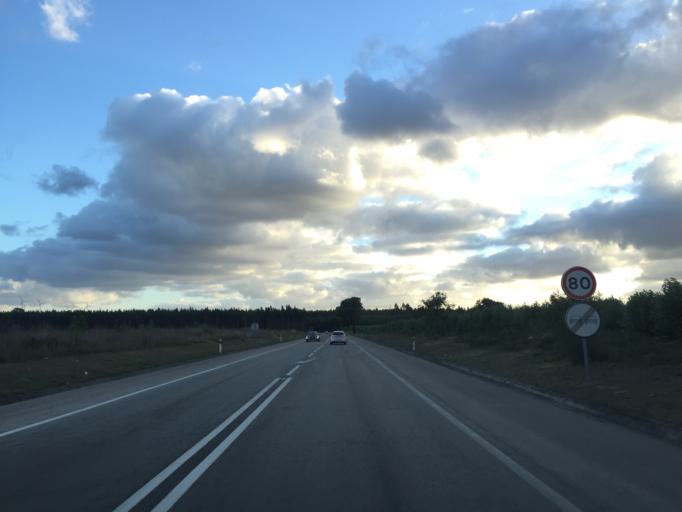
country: PT
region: Leiria
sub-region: Alcobaca
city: Benedita
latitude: 39.4225
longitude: -8.9616
